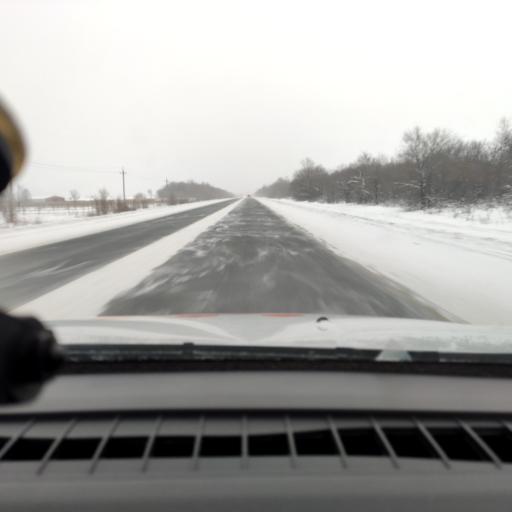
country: RU
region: Samara
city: Kinel'
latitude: 53.2502
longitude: 50.6567
